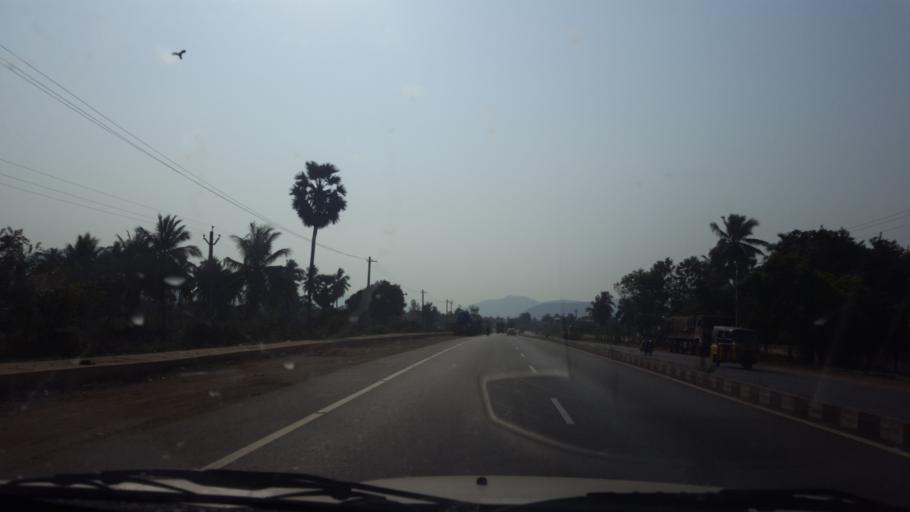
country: IN
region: Andhra Pradesh
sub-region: Vishakhapatnam
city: Anakapalle
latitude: 17.6656
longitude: 82.9513
